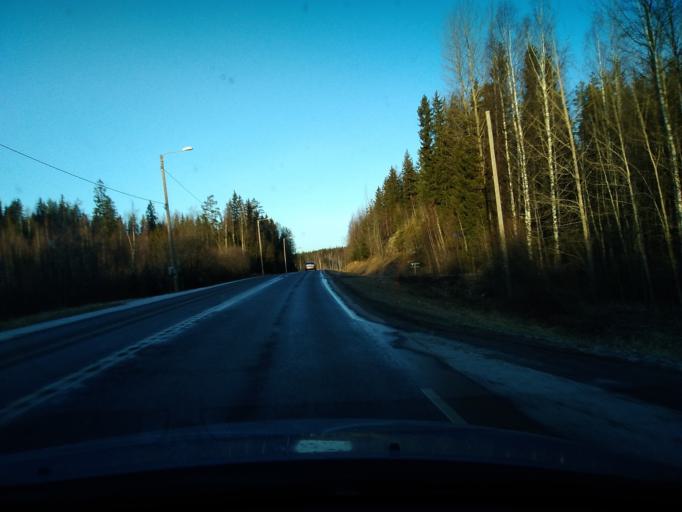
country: FI
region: Haeme
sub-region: Riihimaeki
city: Loppi
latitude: 60.7158
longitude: 24.4679
